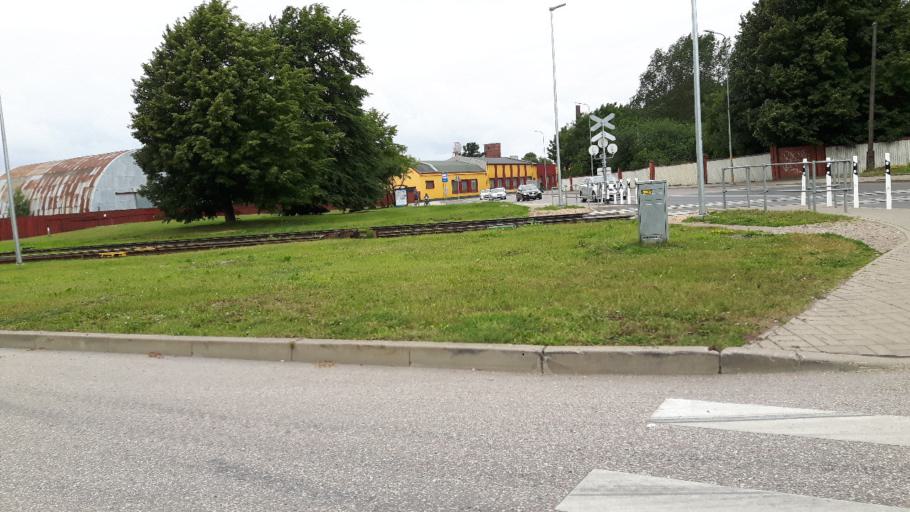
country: LV
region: Liepaja
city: Liepaja
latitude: 56.5211
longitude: 21.0057
